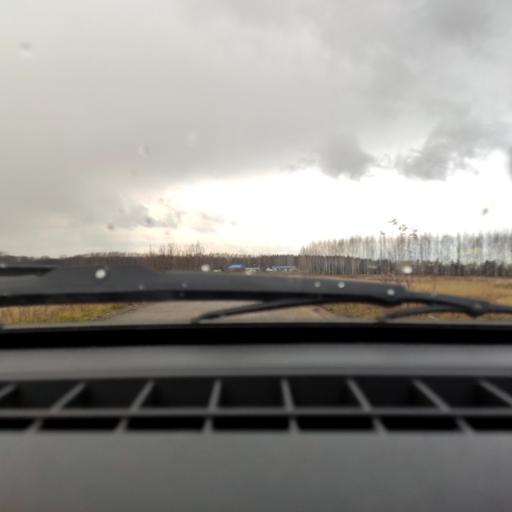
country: RU
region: Bashkortostan
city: Iglino
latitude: 54.7431
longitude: 56.3181
